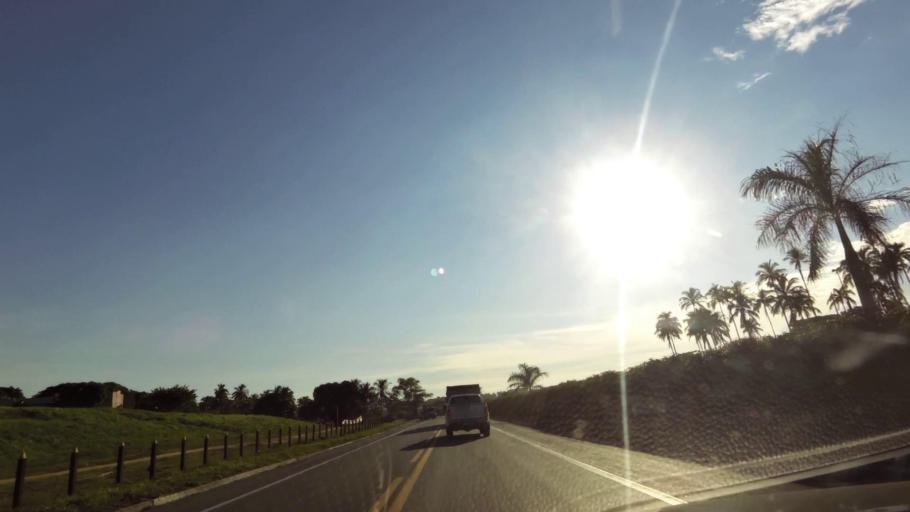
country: BR
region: Espirito Santo
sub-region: Guarapari
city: Guarapari
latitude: -20.6048
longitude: -40.5040
